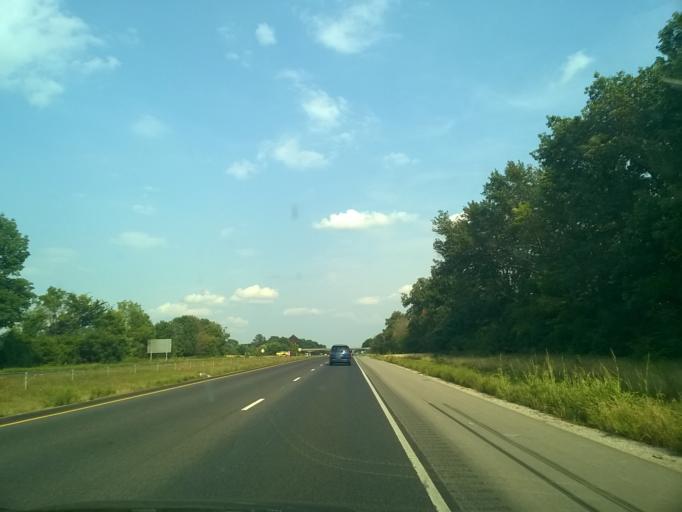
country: US
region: Indiana
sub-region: Vigo County
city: Terre Haute
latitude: 39.4307
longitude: -87.3645
